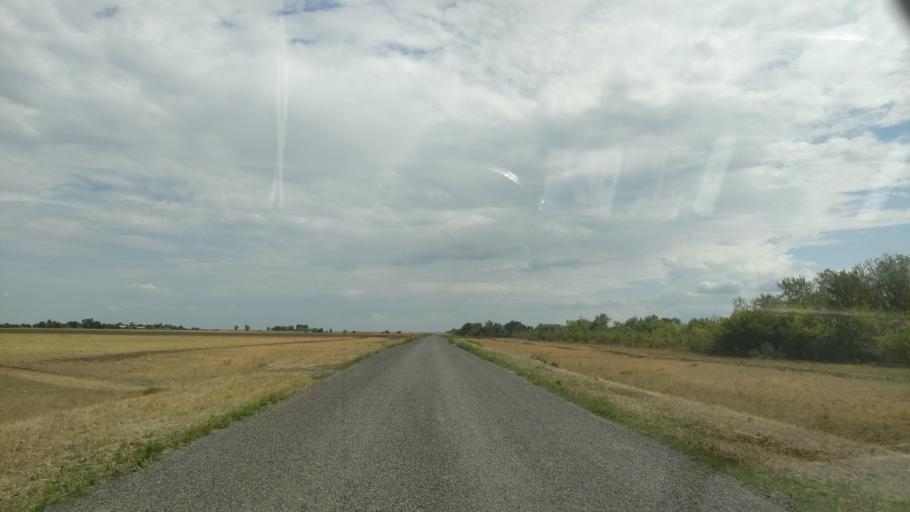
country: KZ
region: Pavlodar
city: Pavlodar
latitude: 52.6392
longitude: 77.0069
